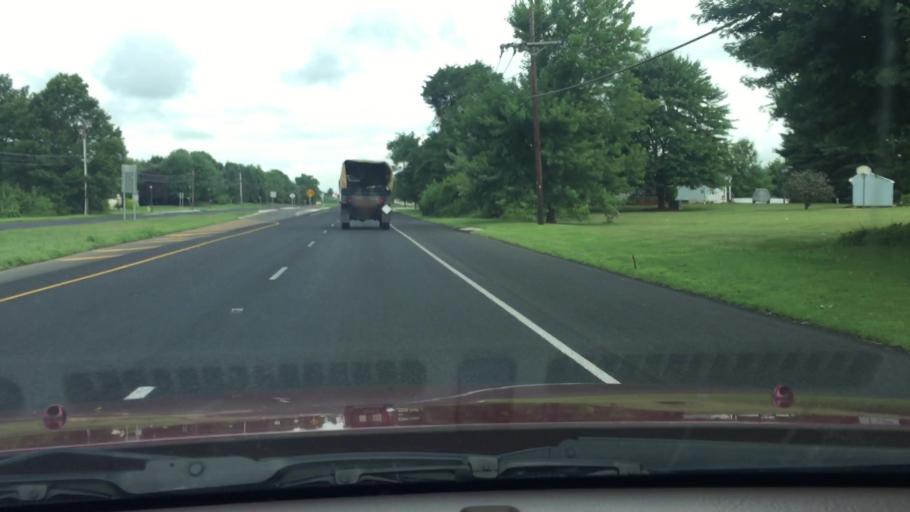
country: US
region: New Jersey
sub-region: Burlington County
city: Fort Dix
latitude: 40.0797
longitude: -74.6655
